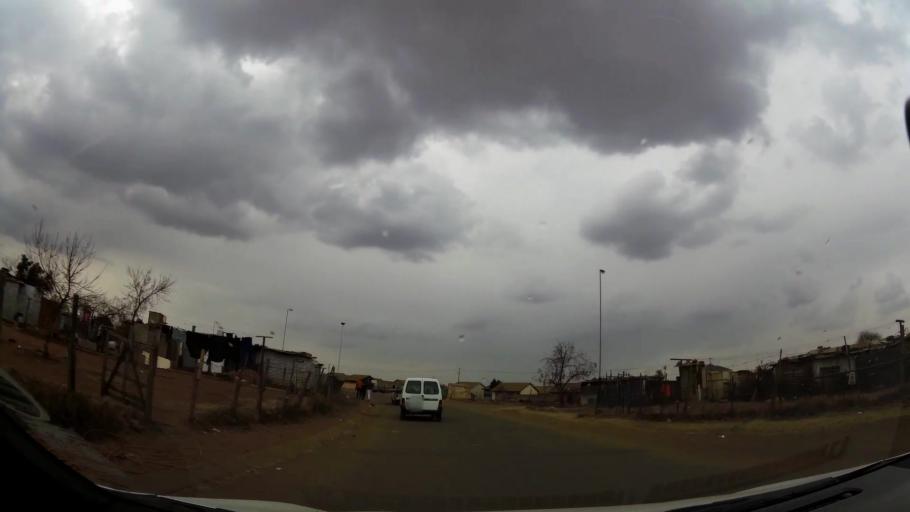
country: ZA
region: Gauteng
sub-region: Ekurhuleni Metropolitan Municipality
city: Germiston
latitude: -26.3629
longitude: 28.1495
